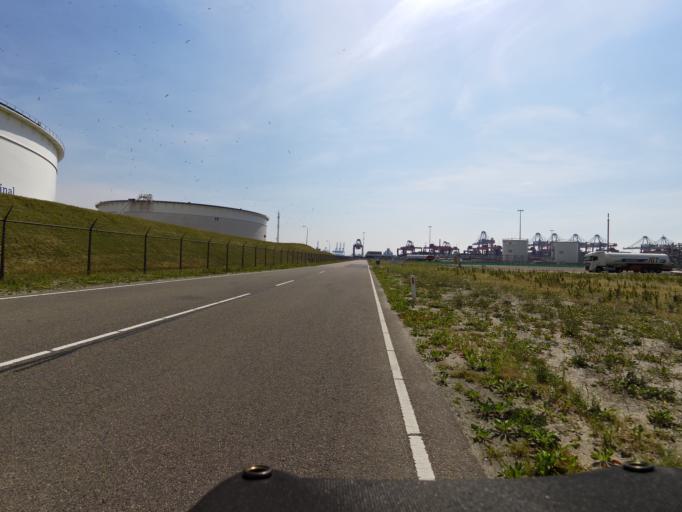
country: NL
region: South Holland
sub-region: Gemeente Rotterdam
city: Hoek van Holland
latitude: 51.9800
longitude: 4.0482
